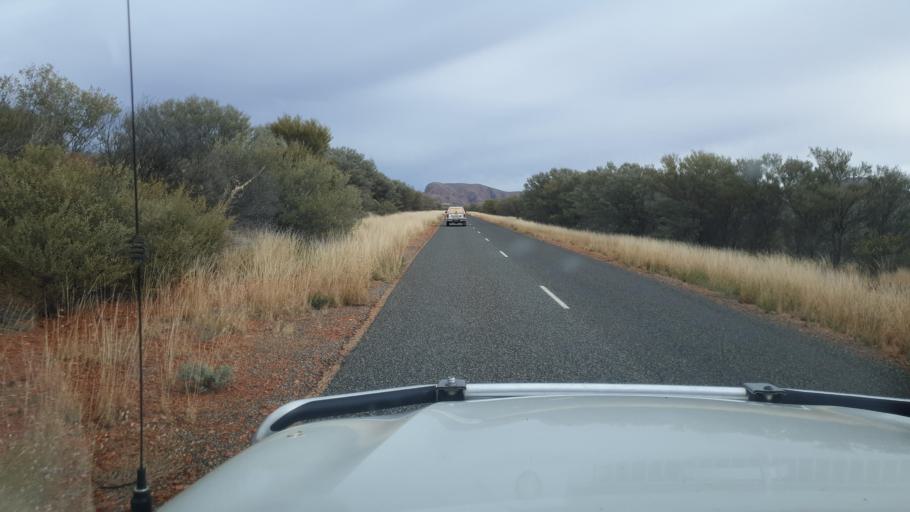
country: AU
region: Northern Territory
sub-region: Alice Springs
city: Alice Springs
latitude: -23.7614
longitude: 133.4988
